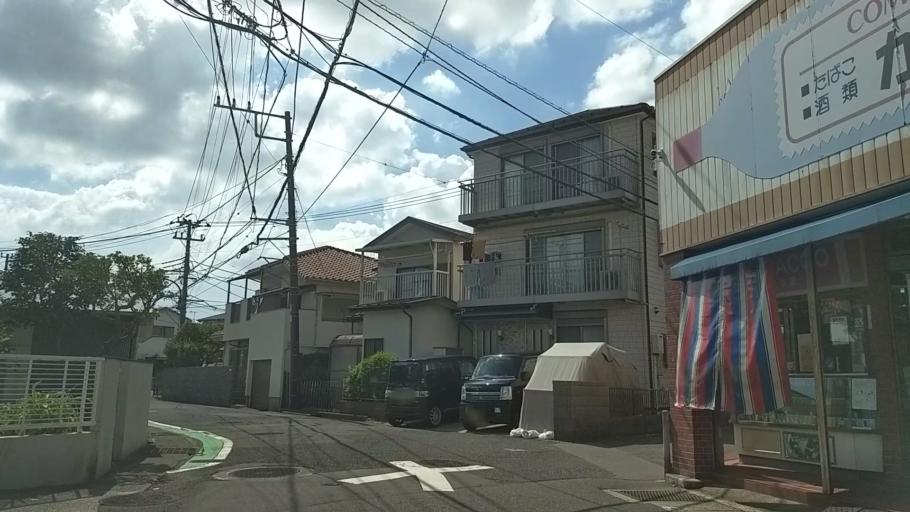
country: JP
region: Kanagawa
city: Miura
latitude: 35.2061
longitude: 139.6247
